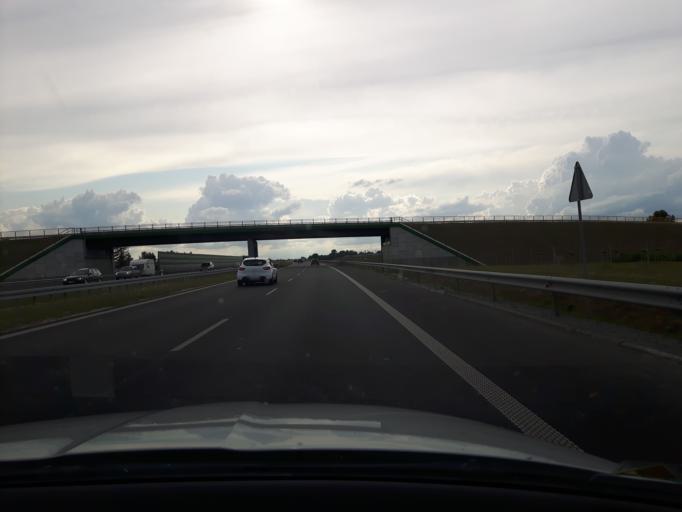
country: PL
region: Warmian-Masurian Voivodeship
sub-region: Powiat elblaski
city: Elblag
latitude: 54.1647
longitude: 19.3321
